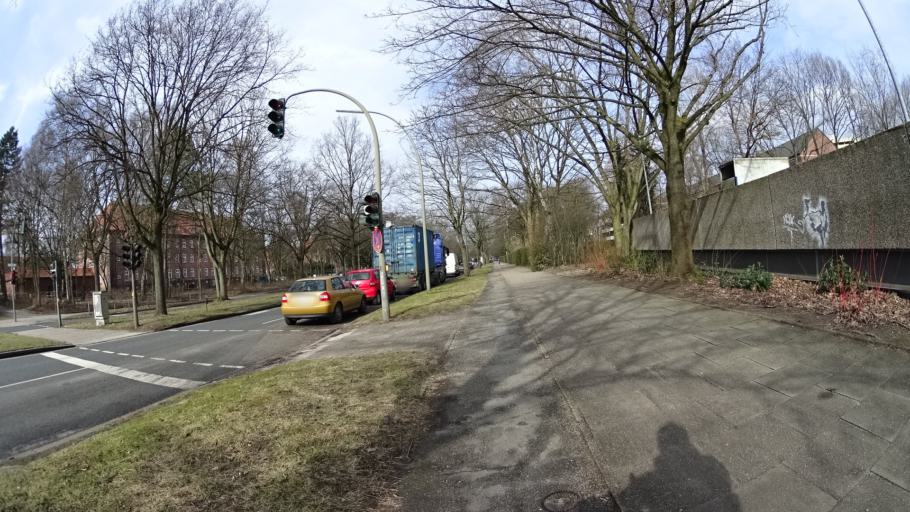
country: DE
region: Hamburg
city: Alsterdorf
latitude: 53.6021
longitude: 10.0134
